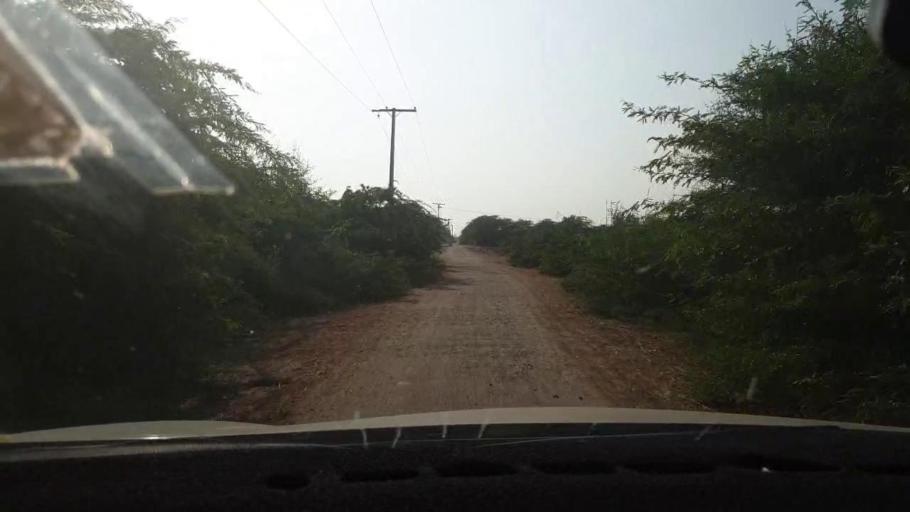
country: PK
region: Sindh
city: Berani
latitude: 25.7502
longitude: 68.7962
